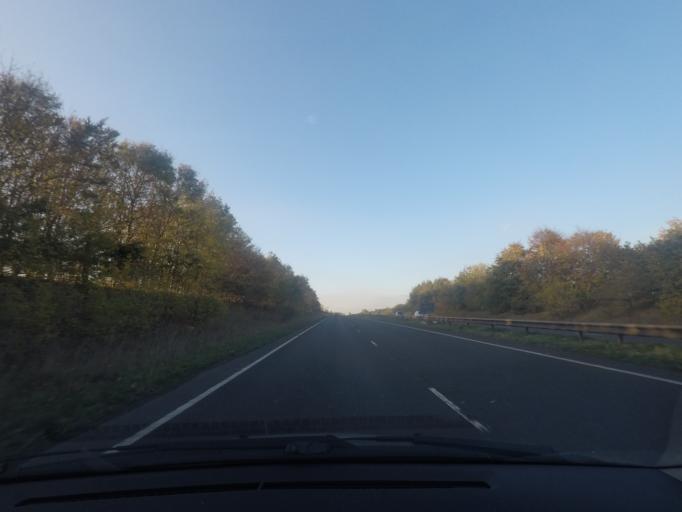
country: GB
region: England
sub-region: North Lincolnshire
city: Barnetby le Wold
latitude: 53.5933
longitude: -0.4181
